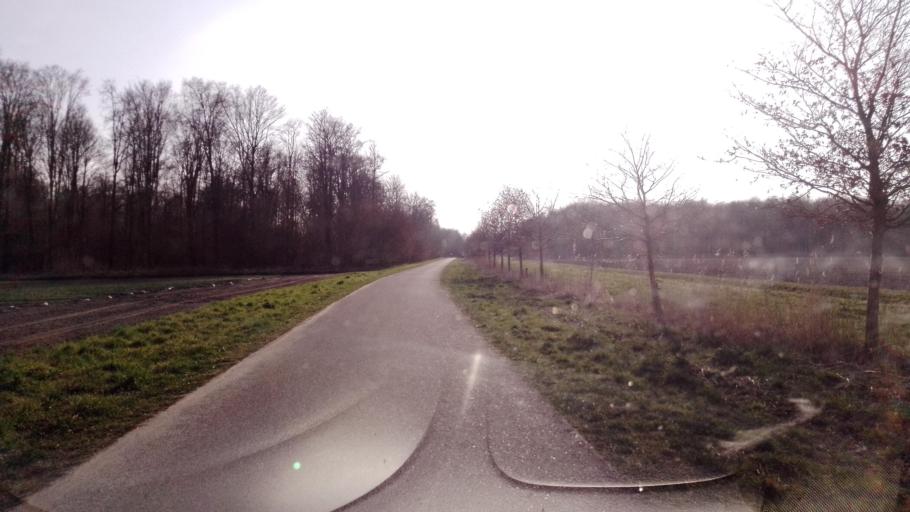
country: NL
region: Gelderland
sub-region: Gemeente Elburg
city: Elburg
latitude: 52.4547
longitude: 5.7812
